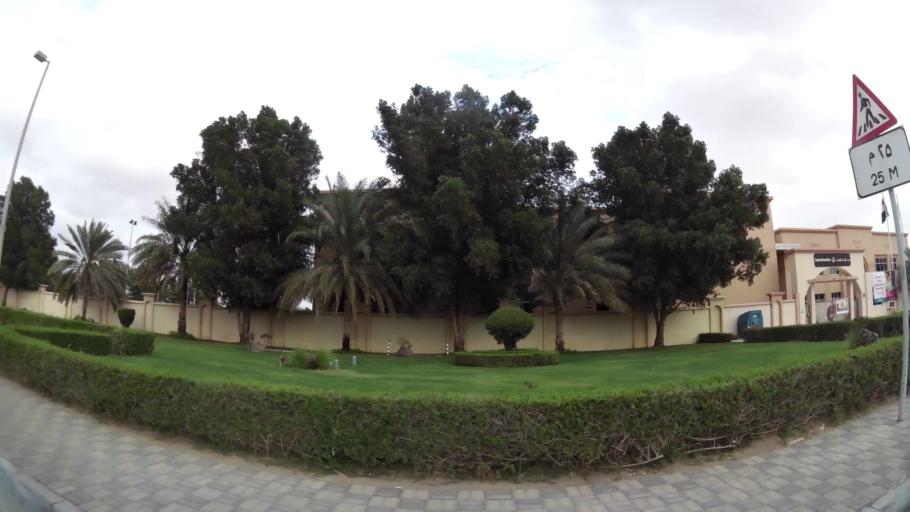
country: AE
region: Abu Dhabi
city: Abu Dhabi
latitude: 24.3631
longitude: 54.5484
